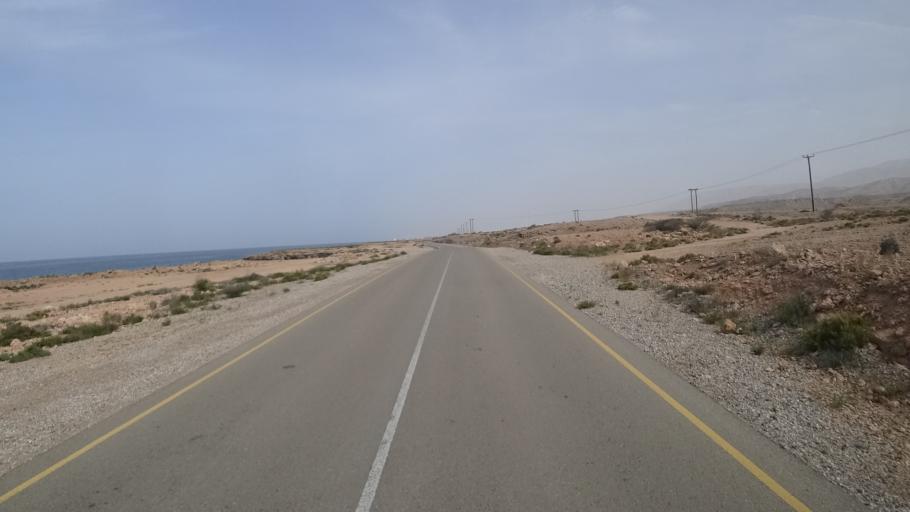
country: OM
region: Ash Sharqiyah
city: Al Qabil
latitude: 23.0113
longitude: 59.1060
